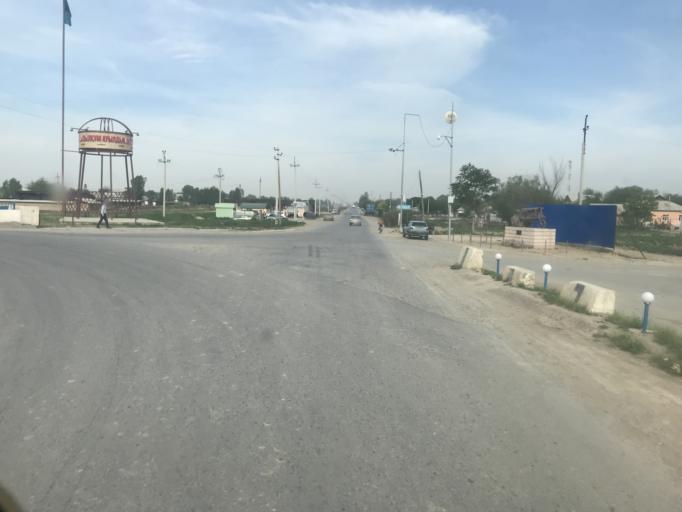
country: KZ
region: Ongtustik Qazaqstan
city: Asykata
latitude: 41.0078
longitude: 68.2161
